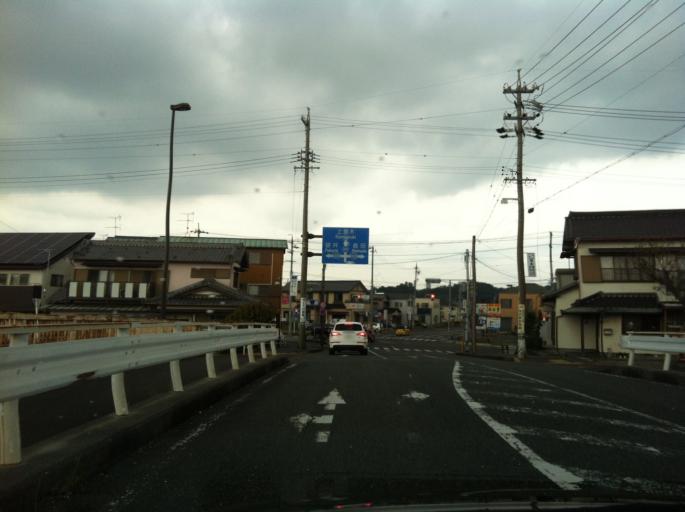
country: JP
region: Shizuoka
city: Kakegawa
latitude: 34.7758
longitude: 138.0021
